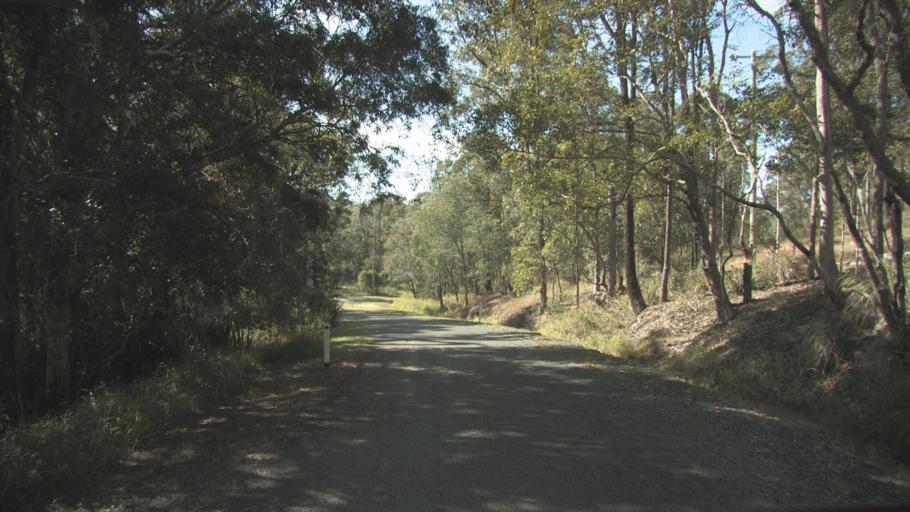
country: AU
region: Queensland
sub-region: Logan
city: Windaroo
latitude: -27.7771
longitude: 153.1745
